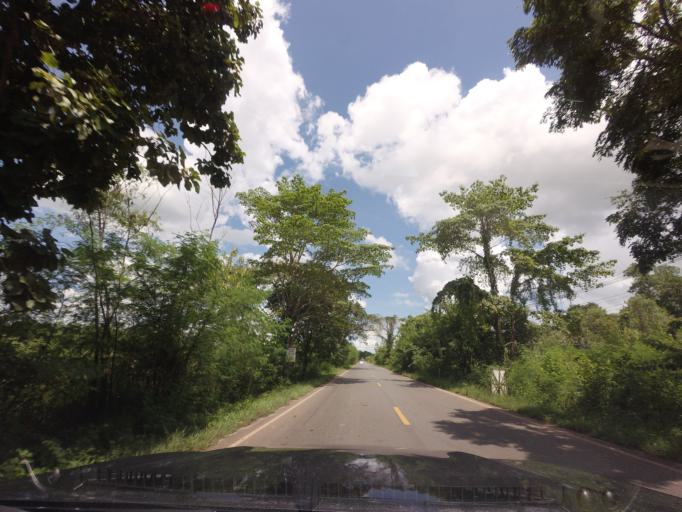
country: TH
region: Changwat Udon Thani
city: Ban Dung
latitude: 17.6735
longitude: 103.1749
